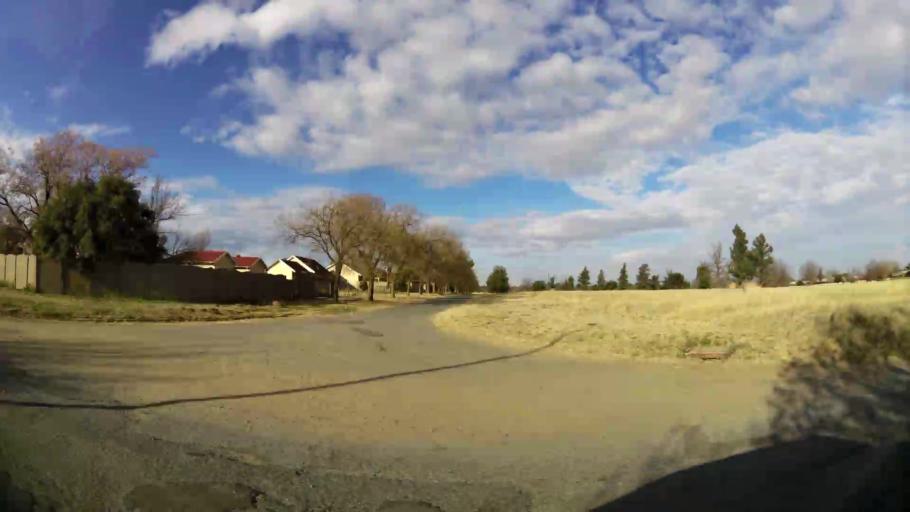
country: ZA
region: Orange Free State
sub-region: Lejweleputswa District Municipality
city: Welkom
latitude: -27.9768
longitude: 26.6961
